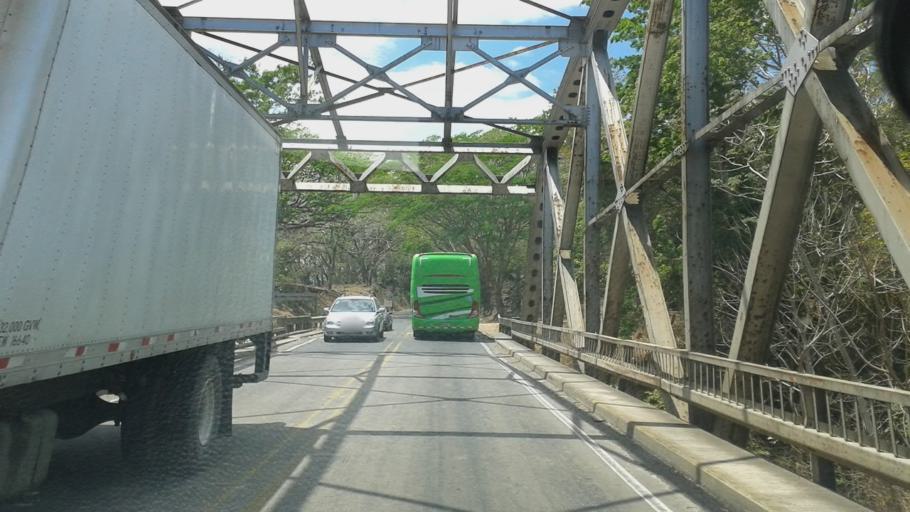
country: CR
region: Puntarenas
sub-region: Canton Central de Puntarenas
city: Puntarenas
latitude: 10.1030
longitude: -84.8743
